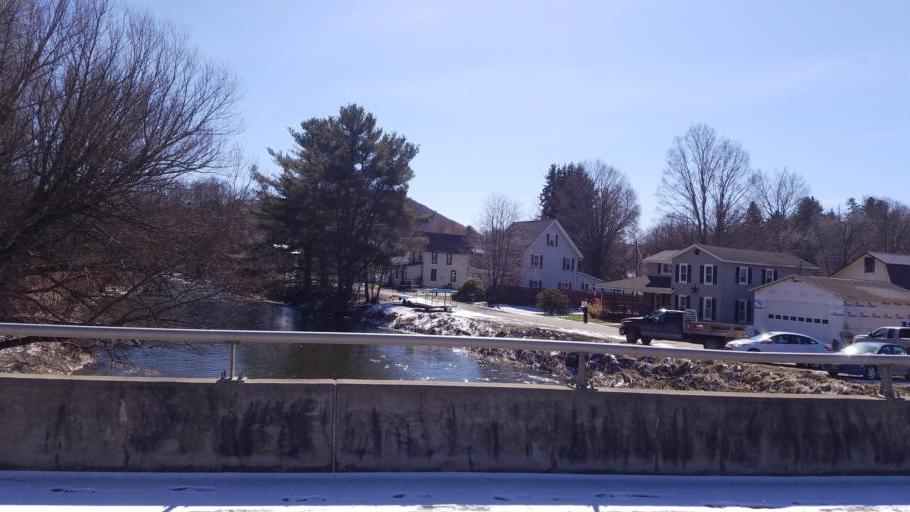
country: US
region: New York
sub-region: Allegany County
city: Wellsville
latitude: 41.9943
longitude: -77.8700
